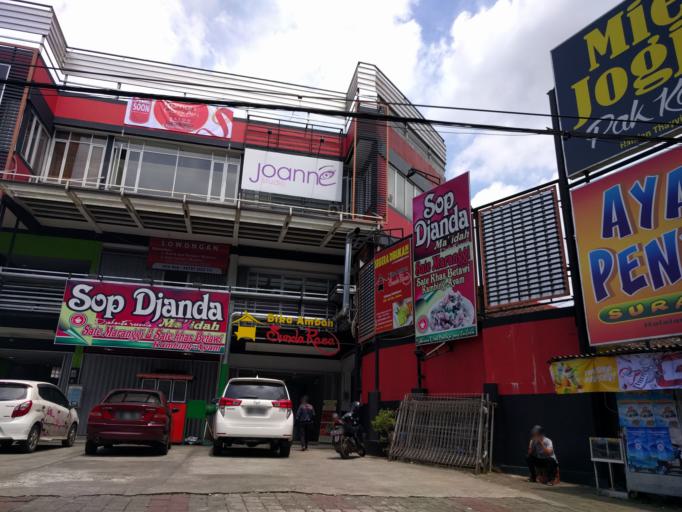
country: ID
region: West Java
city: Bogor
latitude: -6.6151
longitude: 106.8141
